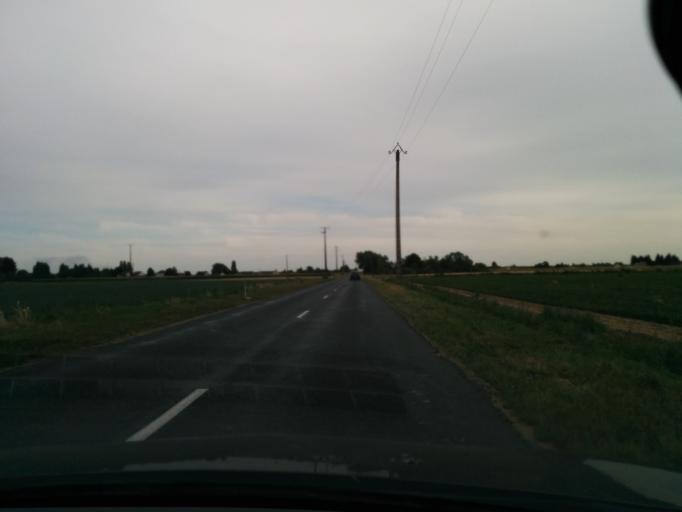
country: FR
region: Centre
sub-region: Departement du Loiret
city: Chateauneuf-sur-Loire
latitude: 47.8419
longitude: 2.2251
